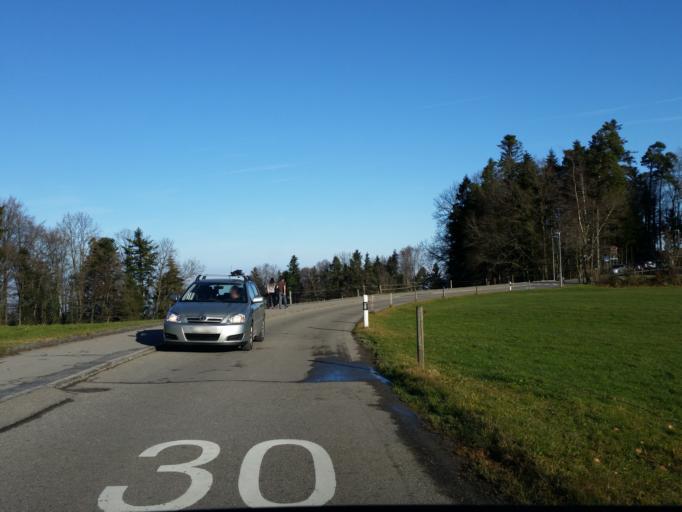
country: CH
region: Saint Gallen
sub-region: Wahlkreis St. Gallen
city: Wittenbach
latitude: 47.4489
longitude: 9.3859
